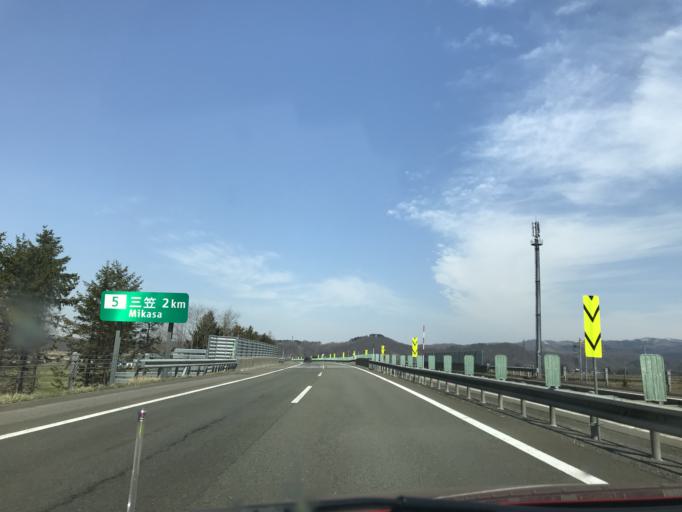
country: JP
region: Hokkaido
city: Iwamizawa
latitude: 43.2242
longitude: 141.8297
